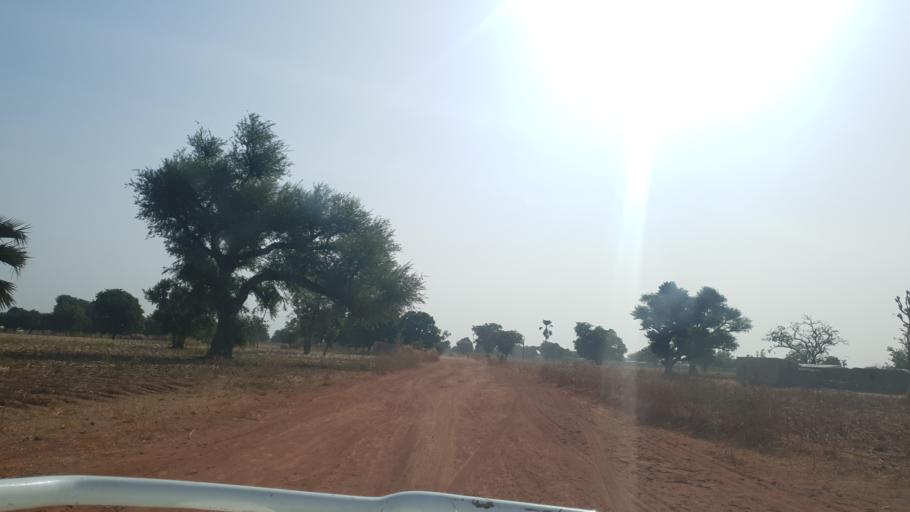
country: ML
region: Koulikoro
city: Dioila
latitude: 12.7071
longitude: -6.7738
